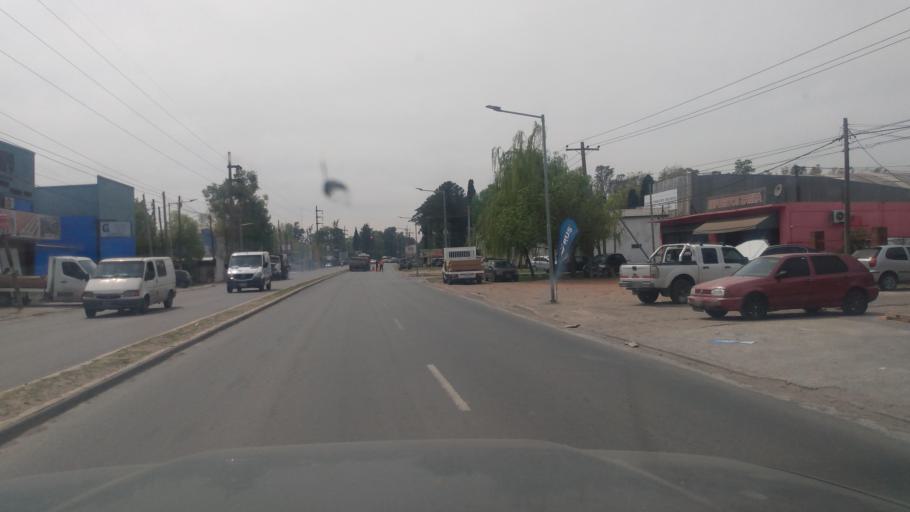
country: AR
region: Buenos Aires
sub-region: Partido de Pilar
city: Pilar
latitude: -34.4447
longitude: -58.9020
